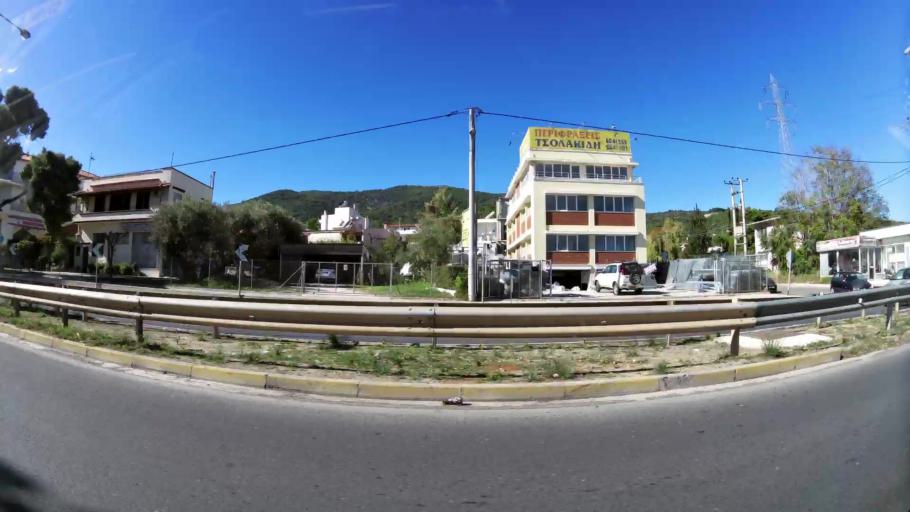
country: GR
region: Attica
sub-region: Nomarchia Anatolikis Attikis
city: Leondarion
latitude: 37.9934
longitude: 23.8484
